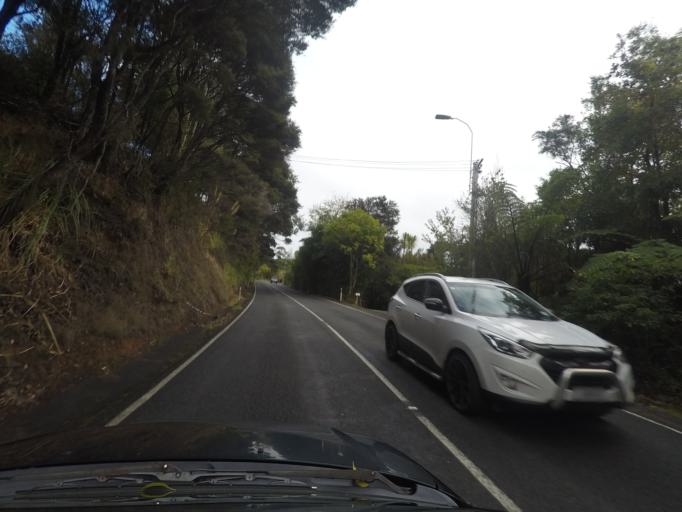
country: NZ
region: Auckland
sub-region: Auckland
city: Waitakere
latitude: -36.8688
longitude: 174.5615
